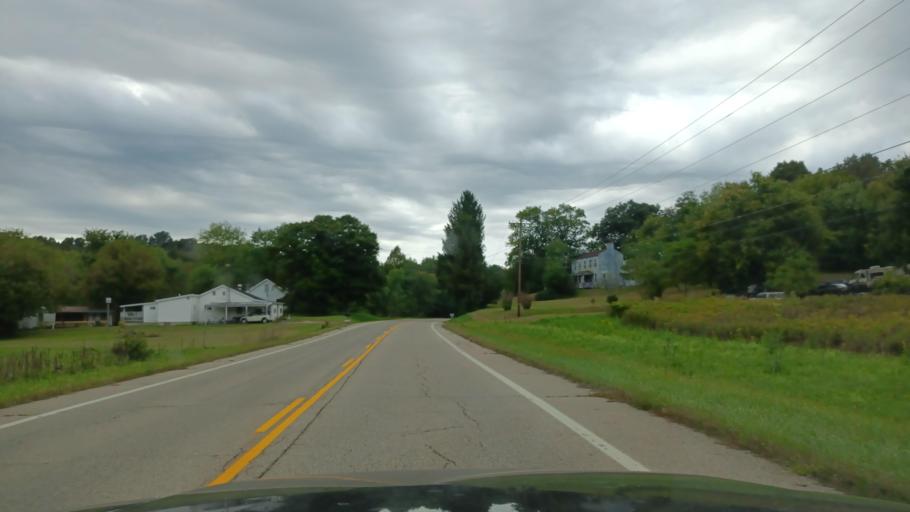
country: US
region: Ohio
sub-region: Vinton County
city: McArthur
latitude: 39.2354
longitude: -82.4449
